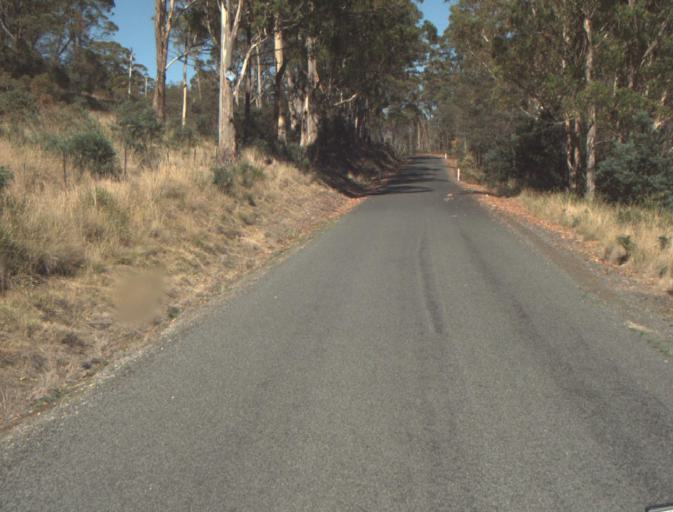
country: AU
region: Tasmania
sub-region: Launceston
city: Newstead
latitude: -41.3676
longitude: 147.3025
